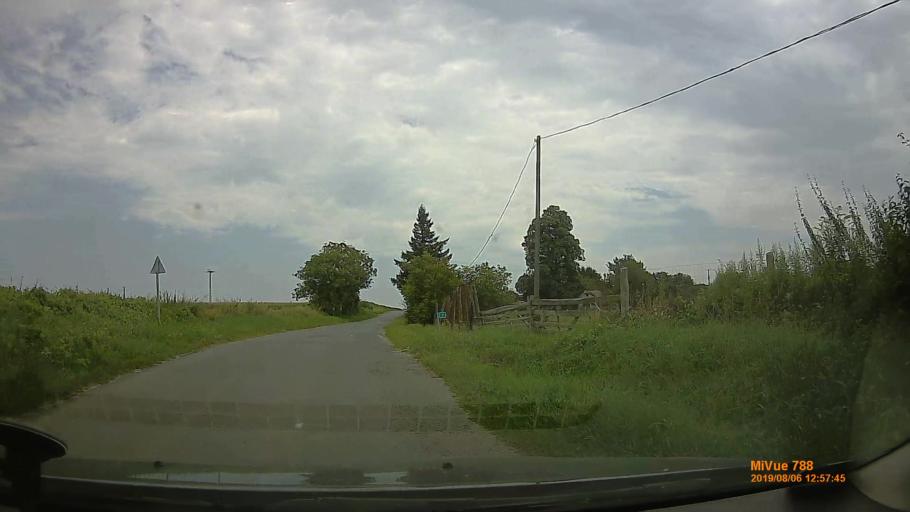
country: HU
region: Zala
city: Pacsa
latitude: 46.6308
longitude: 17.0427
